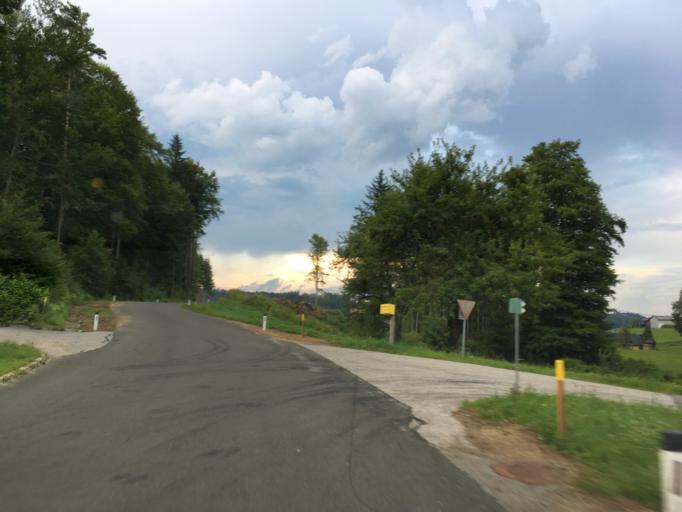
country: AT
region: Styria
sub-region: Politischer Bezirk Leibnitz
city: Oberhaag
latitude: 46.6781
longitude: 15.3527
